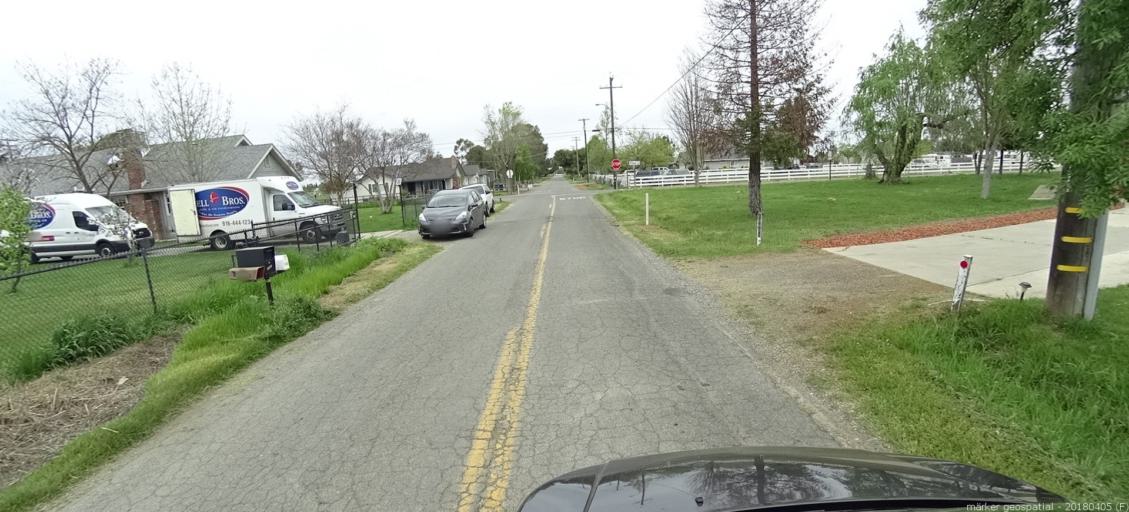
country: US
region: California
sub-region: Sacramento County
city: Galt
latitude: 38.2675
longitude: -121.3261
